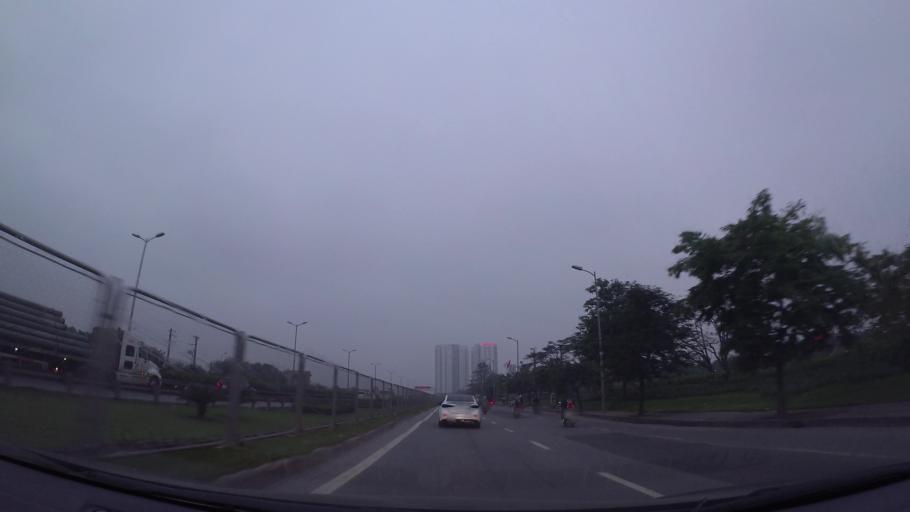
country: VN
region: Ha Noi
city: Van Dien
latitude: 20.9644
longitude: 105.8579
